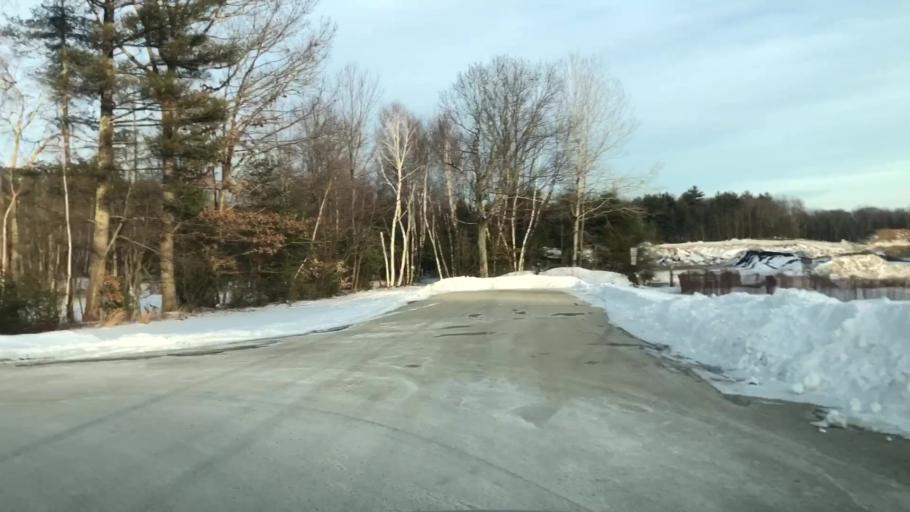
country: US
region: New Hampshire
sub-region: Hillsborough County
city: Milford
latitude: 42.8240
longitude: -71.6921
